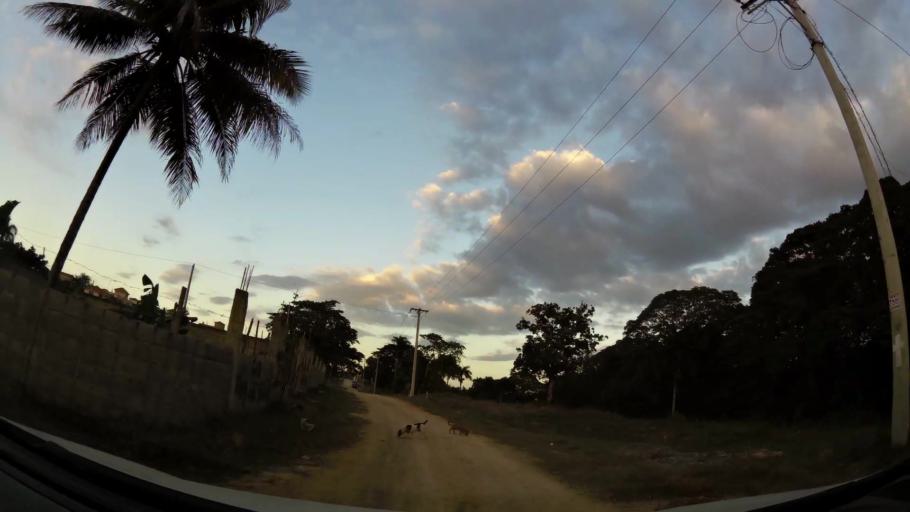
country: DO
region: Nacional
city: La Agustina
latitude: 18.5654
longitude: -69.9417
